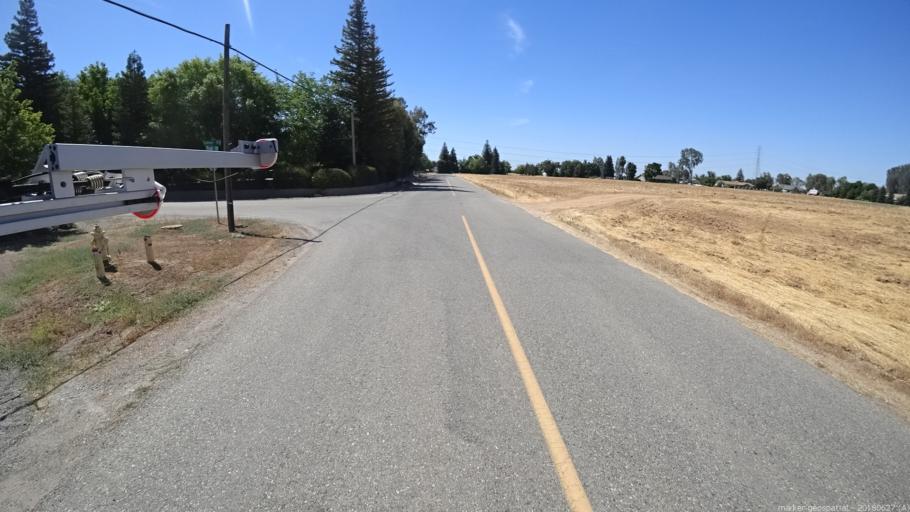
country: US
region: California
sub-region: Madera County
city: Bonadelle Ranchos-Madera Ranchos
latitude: 36.9213
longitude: -119.8756
